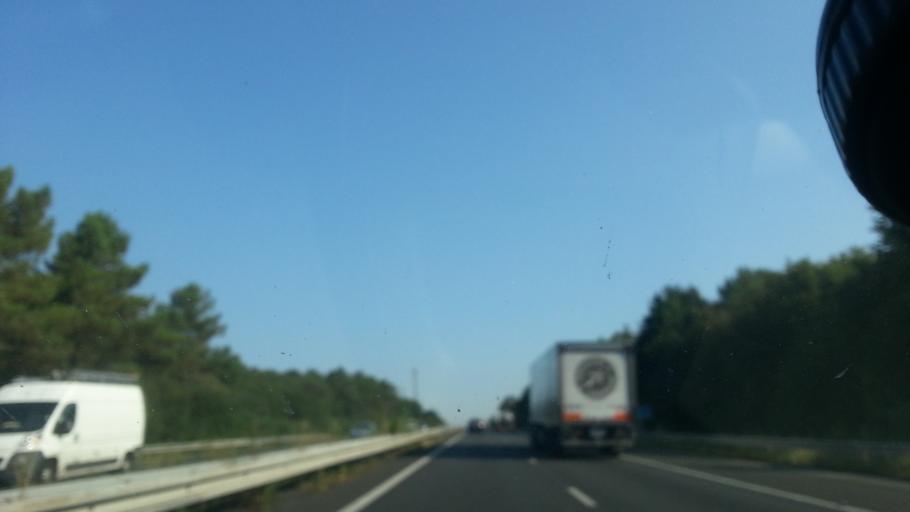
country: FR
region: Poitou-Charentes
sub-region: Departement de la Vienne
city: Les Ormes
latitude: 46.9610
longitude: 0.5489
